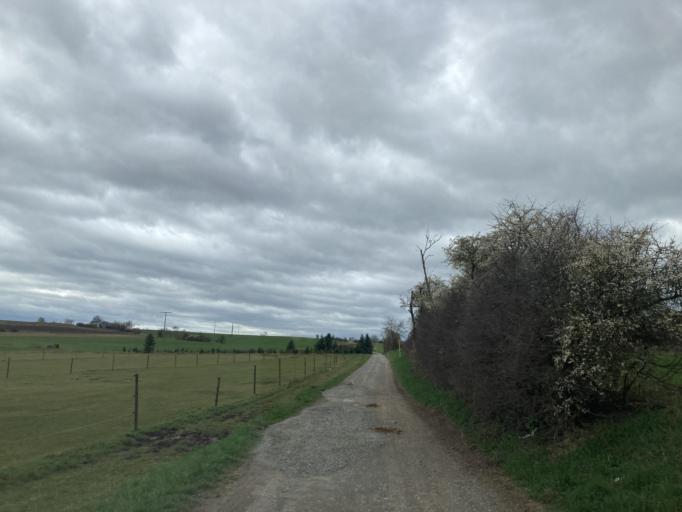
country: DE
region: Baden-Wuerttemberg
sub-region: Tuebingen Region
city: Rottenburg
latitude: 48.5191
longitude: 8.9665
